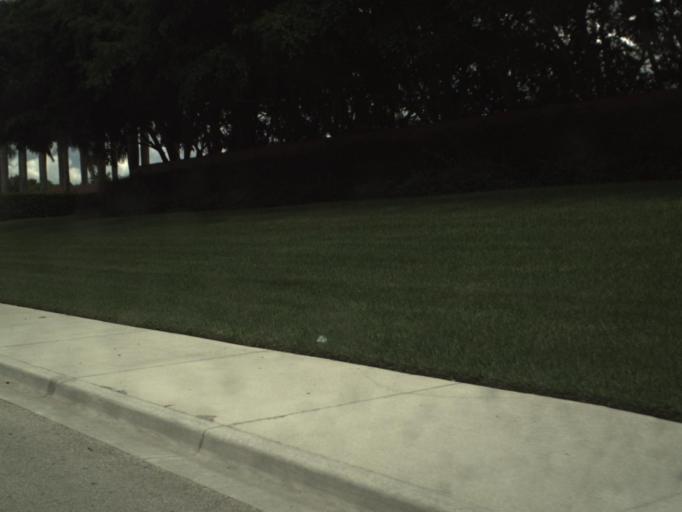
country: US
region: Florida
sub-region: Palm Beach County
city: Wellington
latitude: 26.6509
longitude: -80.1843
